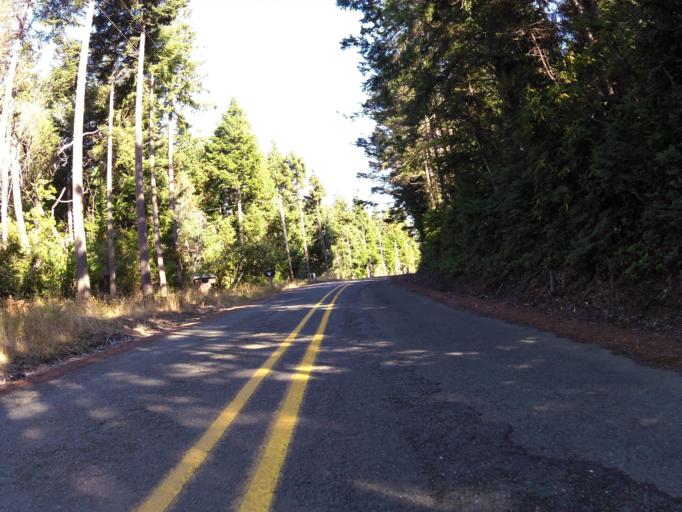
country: US
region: Oregon
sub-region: Coos County
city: Bandon
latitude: 43.0388
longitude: -124.3979
